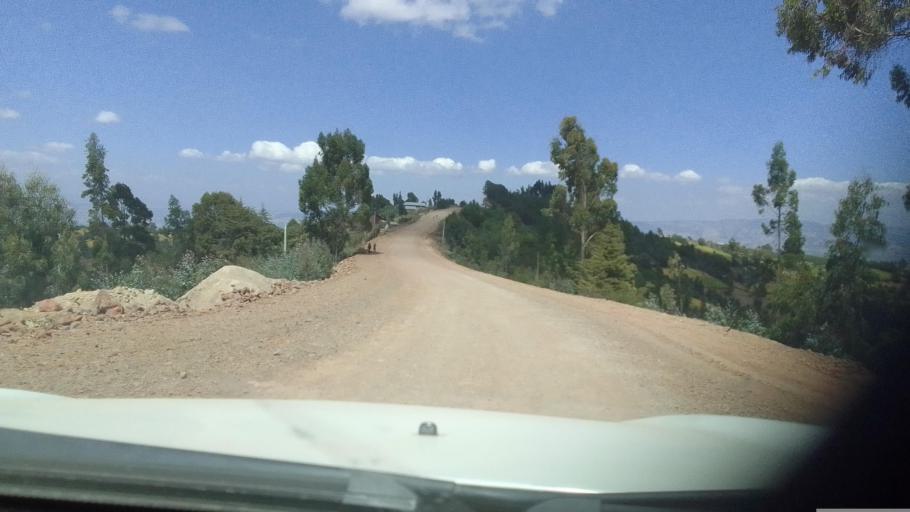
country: ET
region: Oromiya
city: Hagere Hiywet
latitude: 8.8373
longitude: 37.8865
